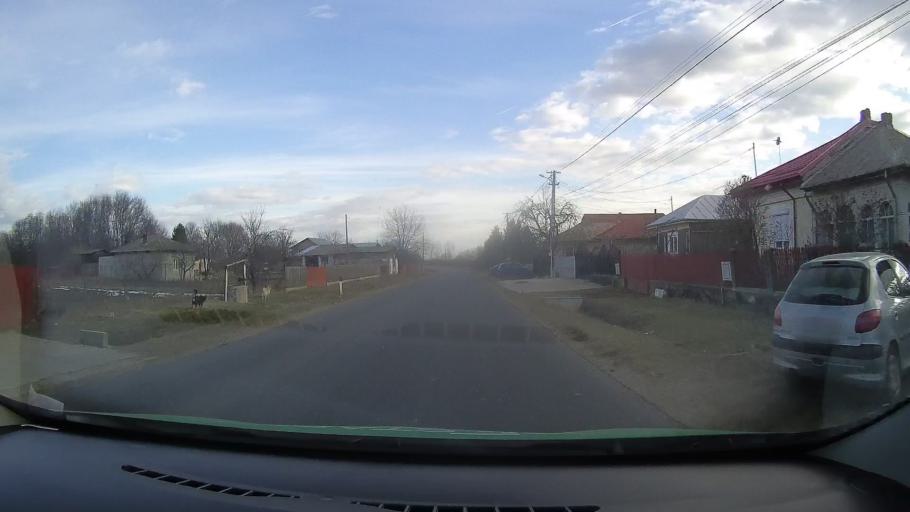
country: RO
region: Dambovita
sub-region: Municipiul Targoviste
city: Targoviste
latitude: 44.8913
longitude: 25.4612
